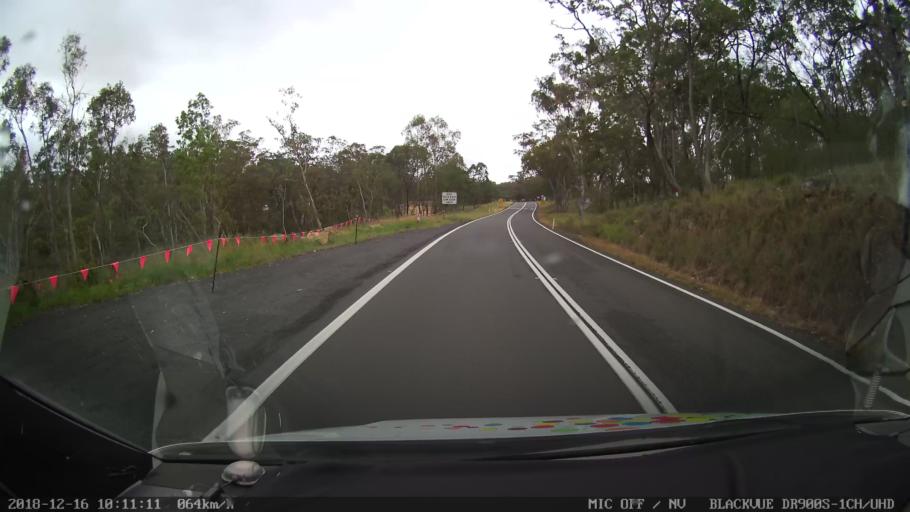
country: AU
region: New South Wales
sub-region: Glen Innes Severn
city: Glen Innes
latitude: -29.3146
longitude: 151.9305
